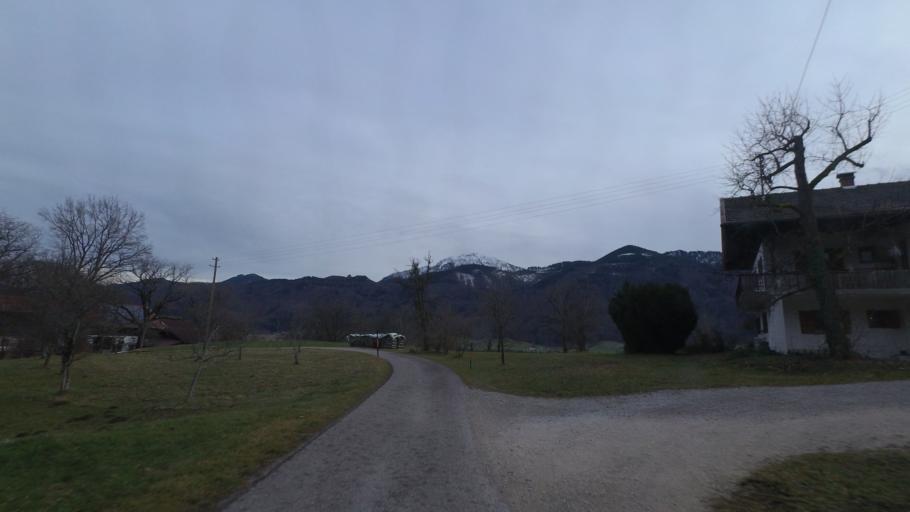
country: DE
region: Bavaria
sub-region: Upper Bavaria
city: Ubersee
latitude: 47.8056
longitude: 12.5181
